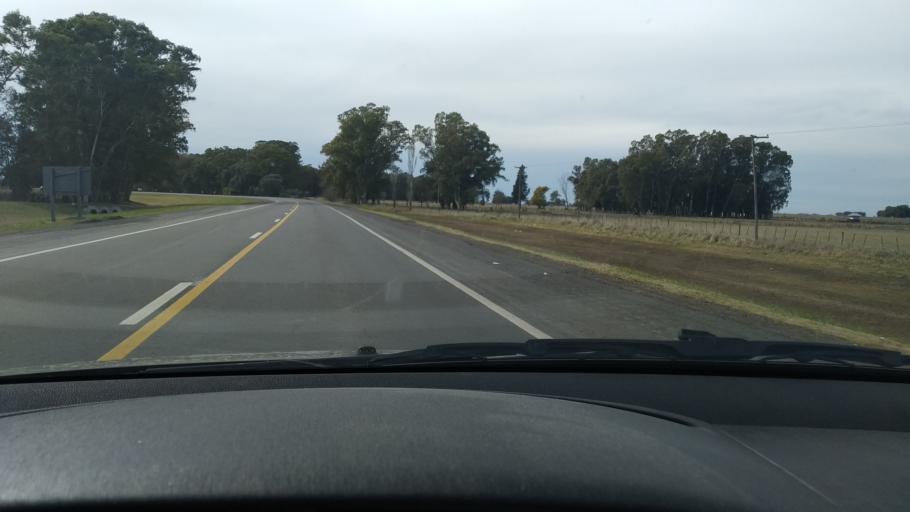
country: AR
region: Buenos Aires
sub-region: Partido de Azul
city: Azul
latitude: -36.7647
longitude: -59.8080
